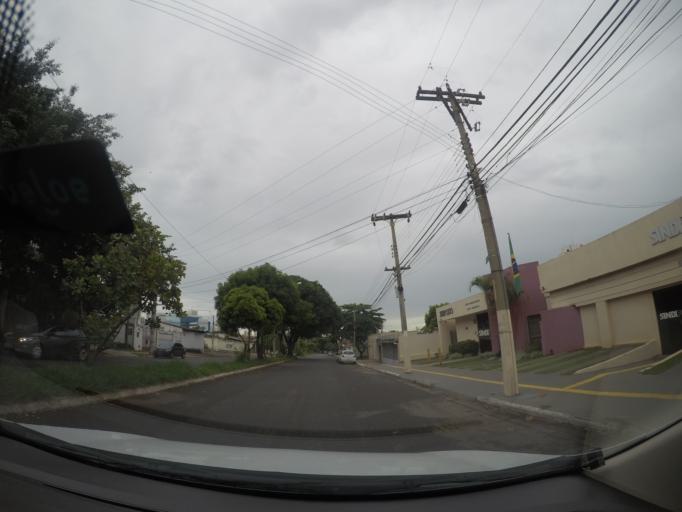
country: BR
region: Goias
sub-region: Goiania
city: Goiania
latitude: -16.6853
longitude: -49.2427
